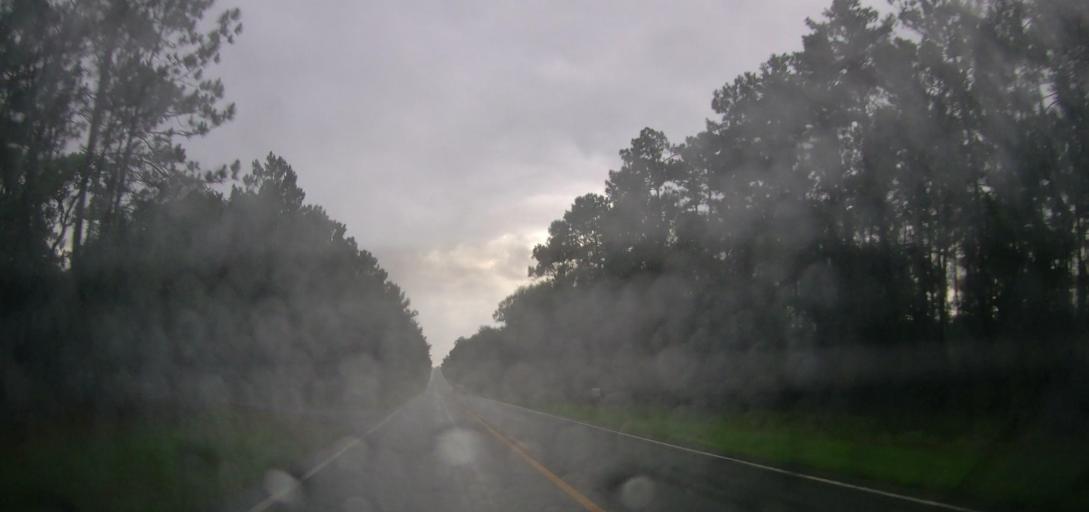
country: US
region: Georgia
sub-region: Brantley County
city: Nahunta
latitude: 31.3274
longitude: -81.7648
